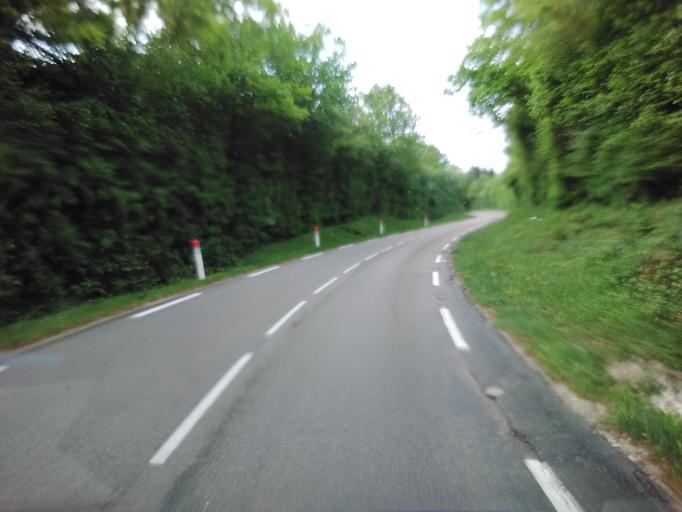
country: FR
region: Franche-Comte
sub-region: Departement du Jura
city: Arbois
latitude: 46.8515
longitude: 5.8173
